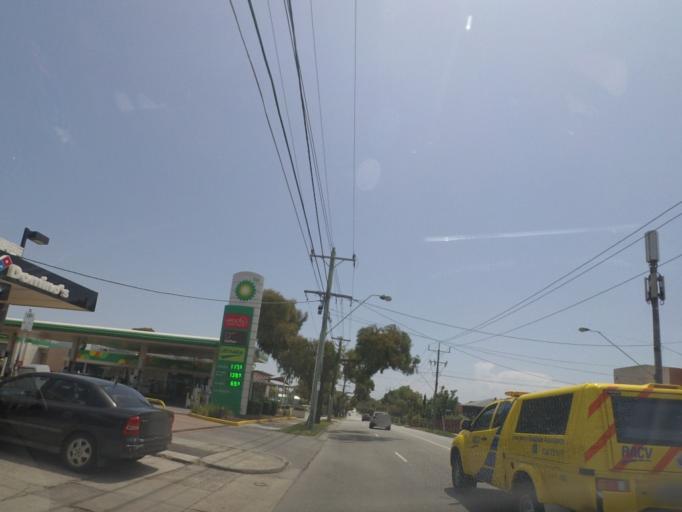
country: AU
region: Victoria
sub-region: Bayside
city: Hampton East
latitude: -37.9460
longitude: 145.0222
